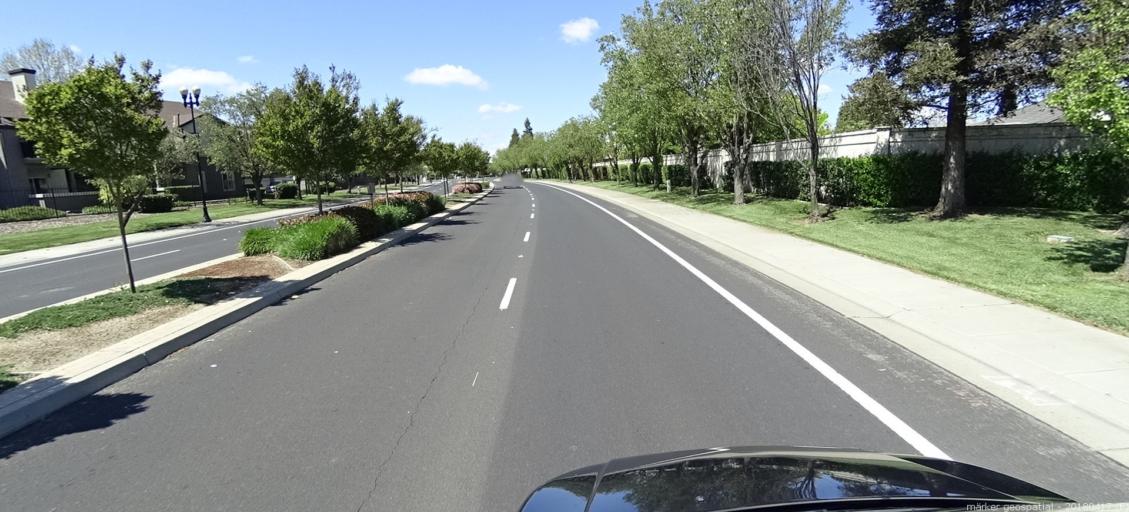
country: US
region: California
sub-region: Sacramento County
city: Laguna
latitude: 38.4120
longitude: -121.4775
